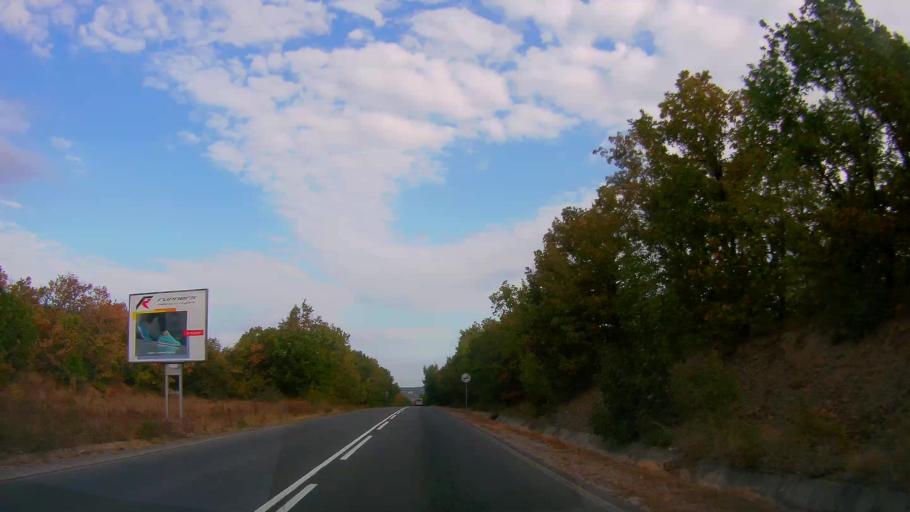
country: BG
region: Burgas
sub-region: Obshtina Sozopol
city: Sozopol
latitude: 42.3385
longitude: 27.7178
